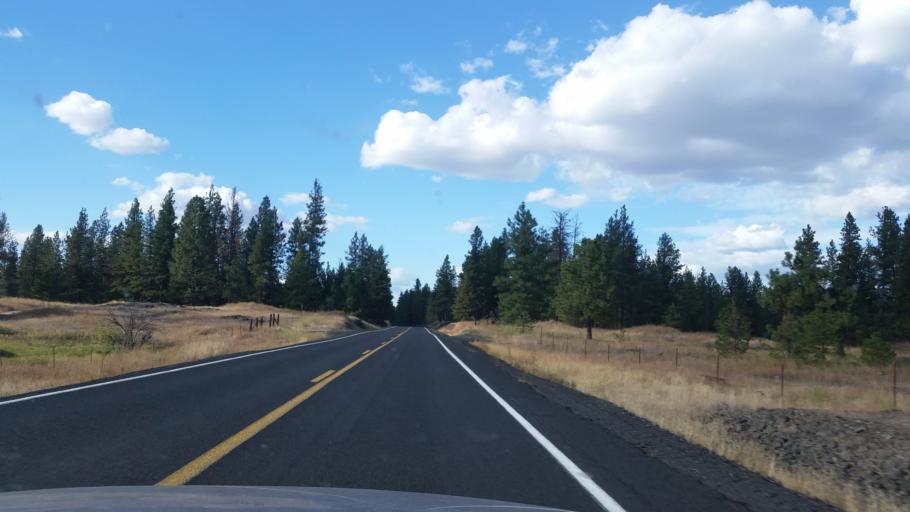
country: US
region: Washington
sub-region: Spokane County
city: Cheney
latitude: 47.4458
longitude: -117.5756
